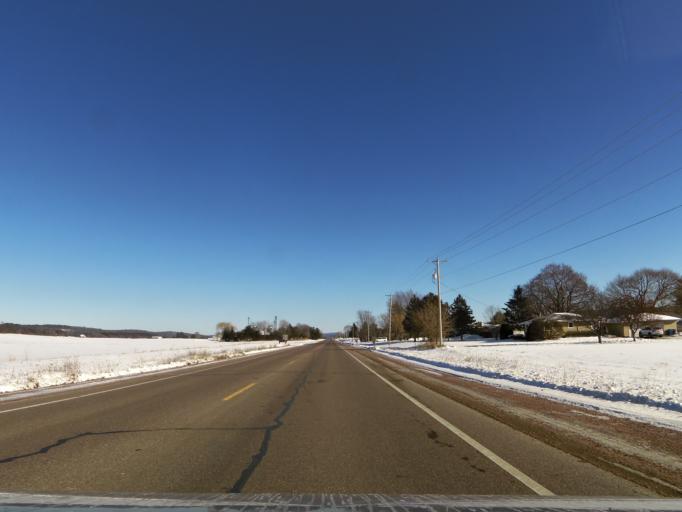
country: US
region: Wisconsin
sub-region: Sauk County
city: Baraboo
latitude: 43.4744
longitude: -89.7109
